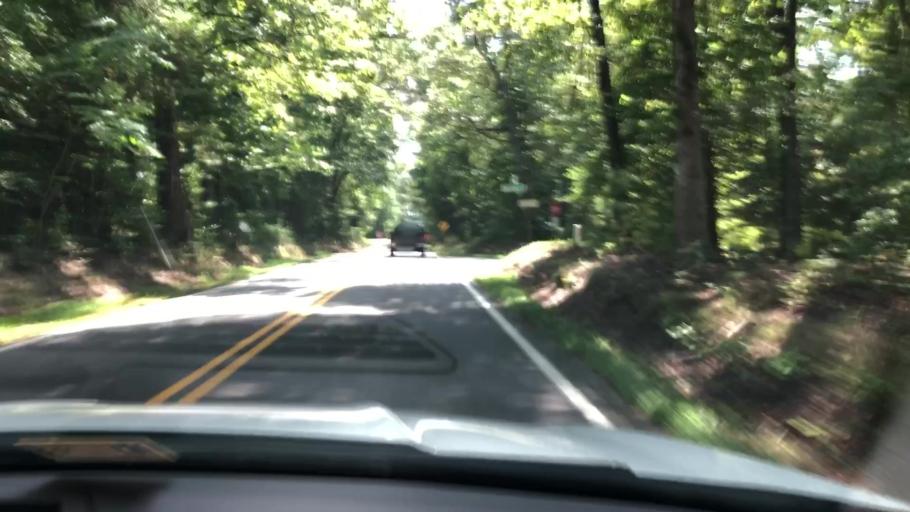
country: US
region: Virginia
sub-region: King William County
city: West Point
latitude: 37.4630
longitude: -76.8390
